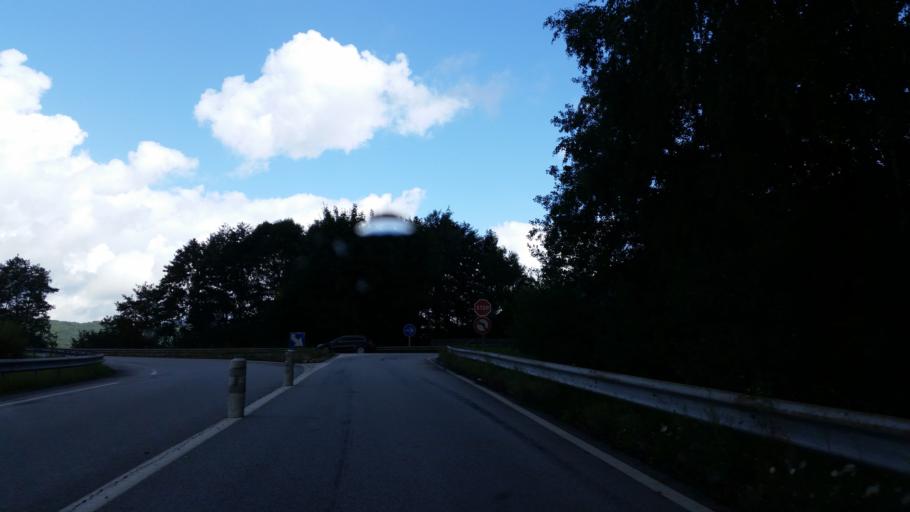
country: FR
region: Lorraine
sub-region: Departement des Vosges
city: Saint-Etienne-les-Remiremont
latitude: 48.0149
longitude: 6.6110
